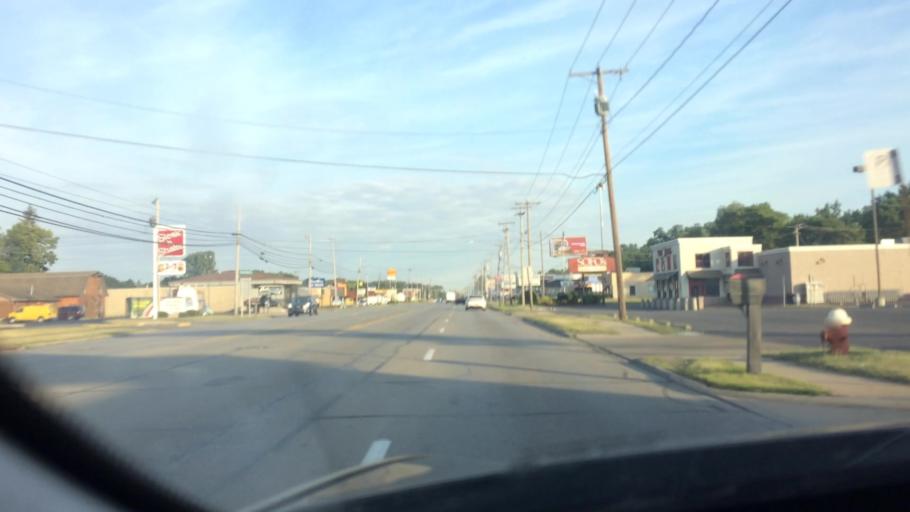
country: US
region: Ohio
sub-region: Lucas County
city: Ottawa Hills
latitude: 41.7045
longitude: -83.6601
